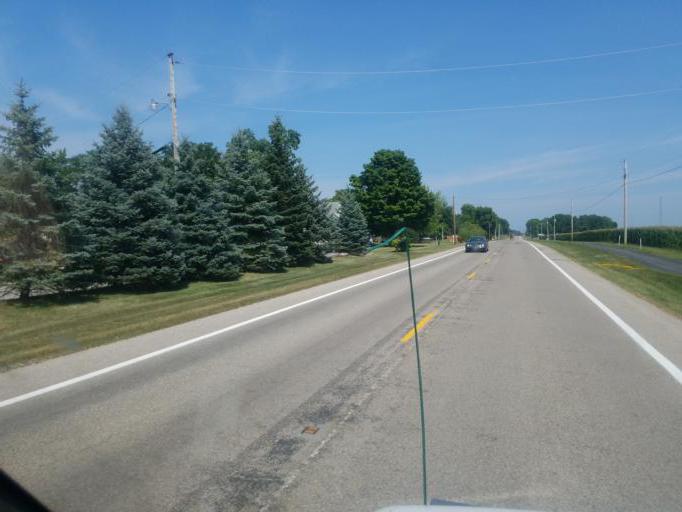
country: US
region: Ohio
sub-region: Mercer County
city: Celina
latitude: 40.5019
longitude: -84.5369
